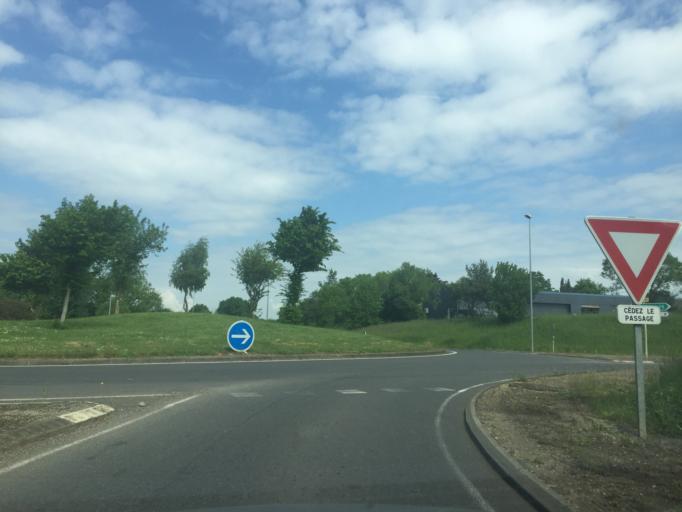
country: FR
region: Poitou-Charentes
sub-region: Departement de la Vienne
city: Lusignan
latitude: 46.4276
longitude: 0.1269
